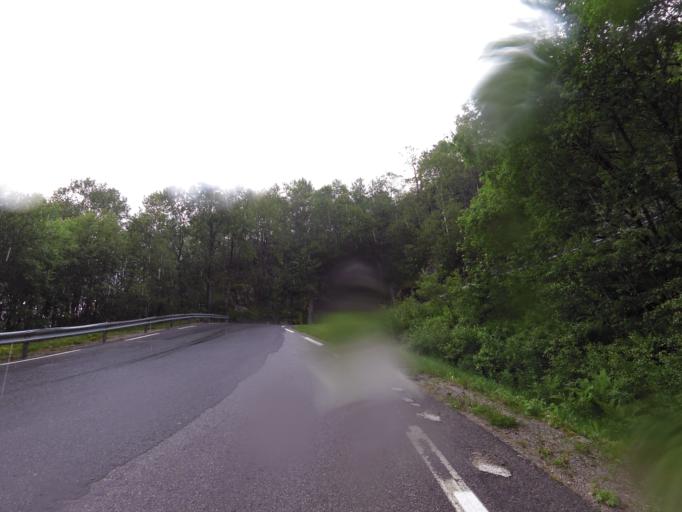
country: NO
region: Vest-Agder
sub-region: Lyngdal
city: Lyngdal
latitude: 58.1127
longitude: 7.0835
